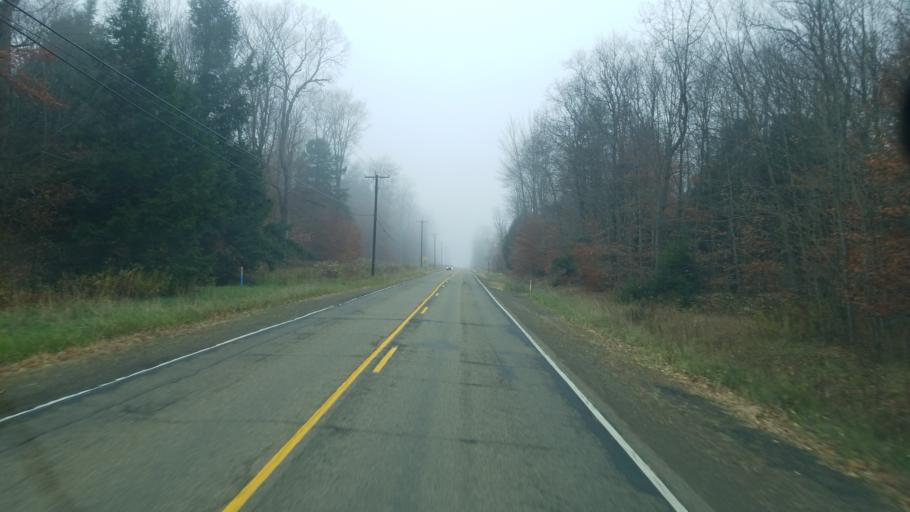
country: US
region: Pennsylvania
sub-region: McKean County
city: Smethport
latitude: 41.8142
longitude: -78.5507
